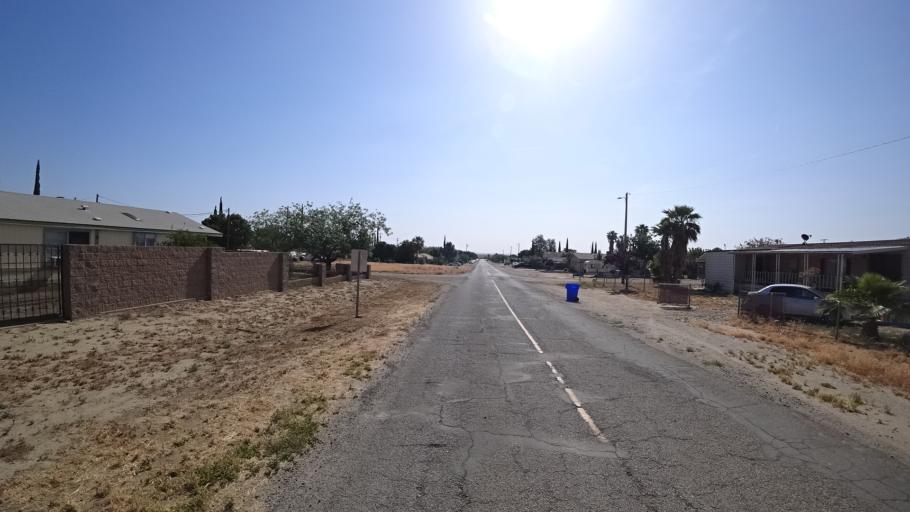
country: US
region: California
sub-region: Kings County
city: Kettleman City
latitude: 36.0103
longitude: -119.9675
